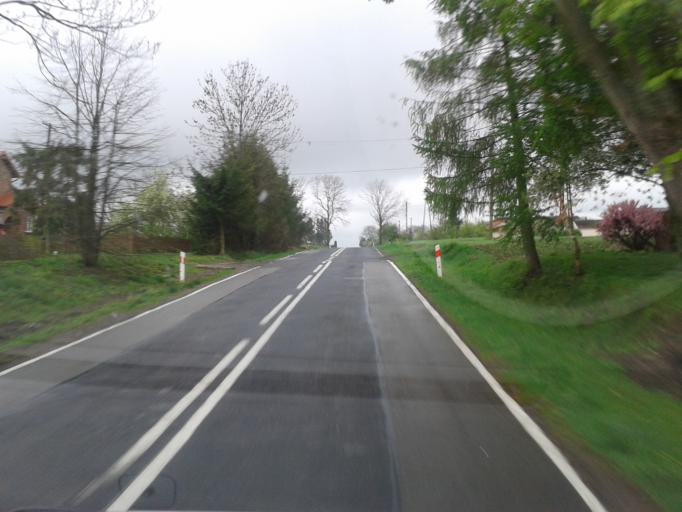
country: PL
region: Lublin Voivodeship
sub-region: Powiat hrubieszowski
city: Dolhobyczow
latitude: 50.5792
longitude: 23.9669
